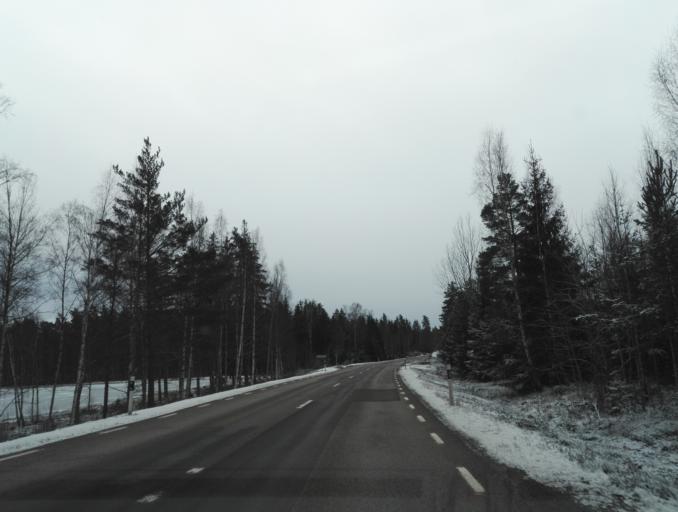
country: SE
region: Kalmar
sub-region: Hultsfreds Kommun
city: Virserum
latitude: 57.2782
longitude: 15.5697
